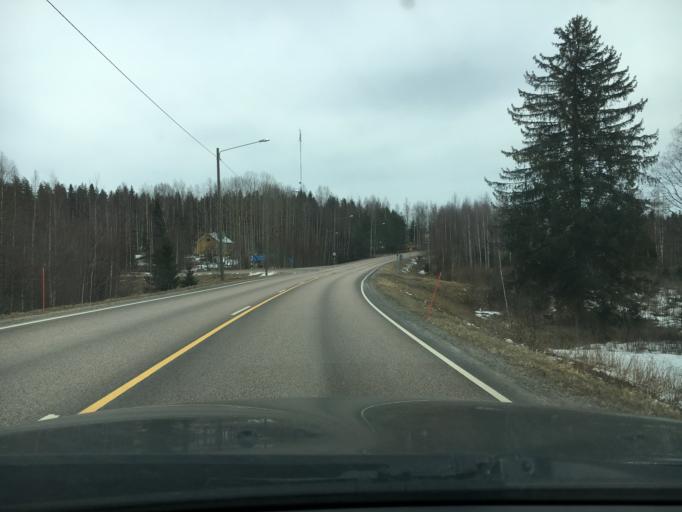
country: FI
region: Central Finland
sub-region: AEaenekoski
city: Konnevesi
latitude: 62.7032
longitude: 26.4597
